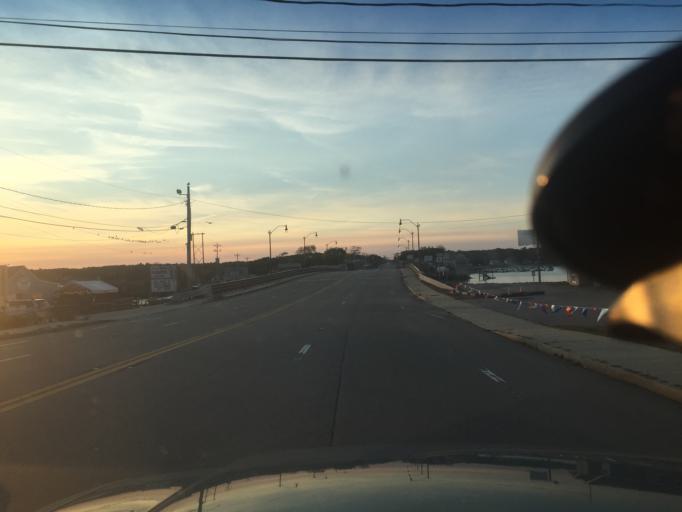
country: US
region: Massachusetts
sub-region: Barnstable County
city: Buzzards Bay
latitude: 41.7465
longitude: -70.6196
